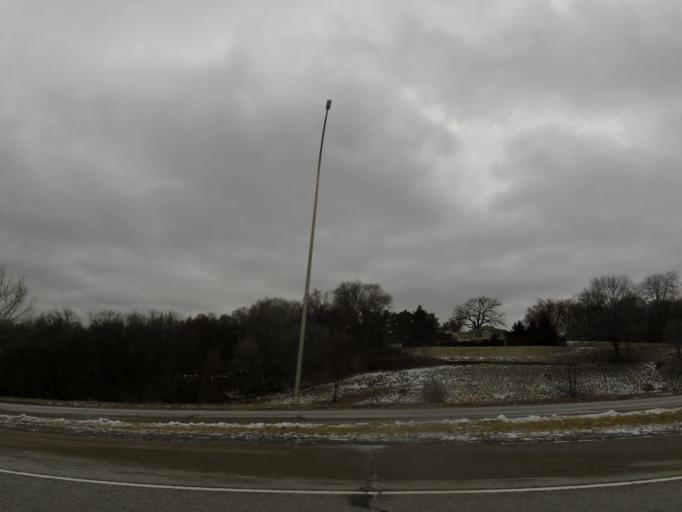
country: US
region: Minnesota
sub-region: Hennepin County
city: Bloomington
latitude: 44.8379
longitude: -93.2421
